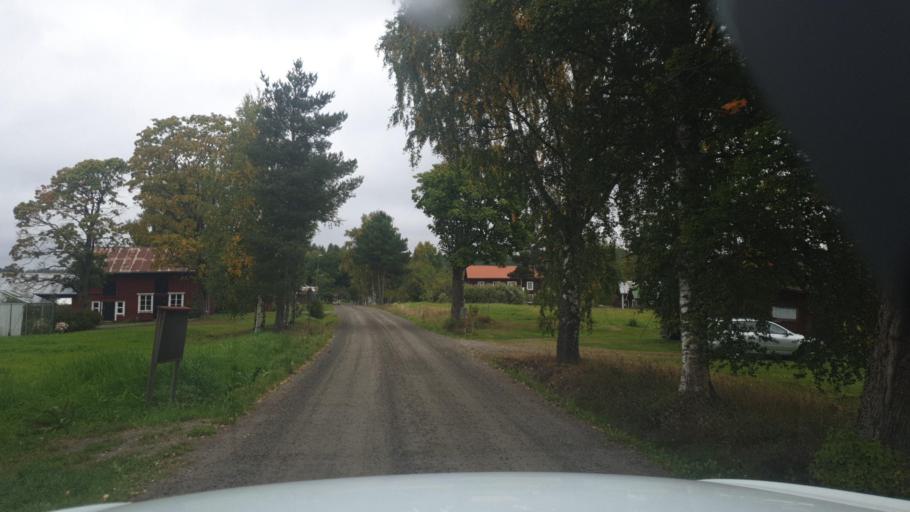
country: SE
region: Vaermland
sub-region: Sunne Kommun
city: Sunne
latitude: 59.8129
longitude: 13.0571
